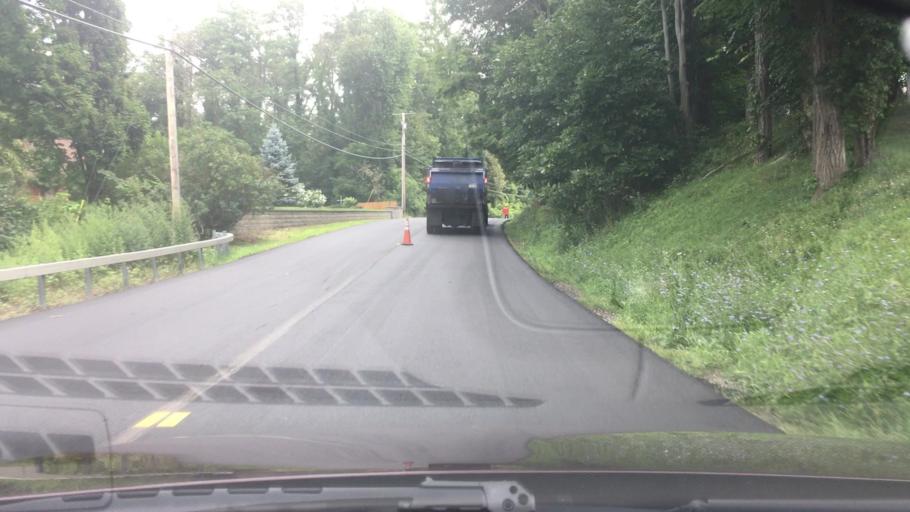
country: US
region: New York
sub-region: Dutchess County
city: Hillside Lake
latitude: 41.5798
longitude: -73.7339
